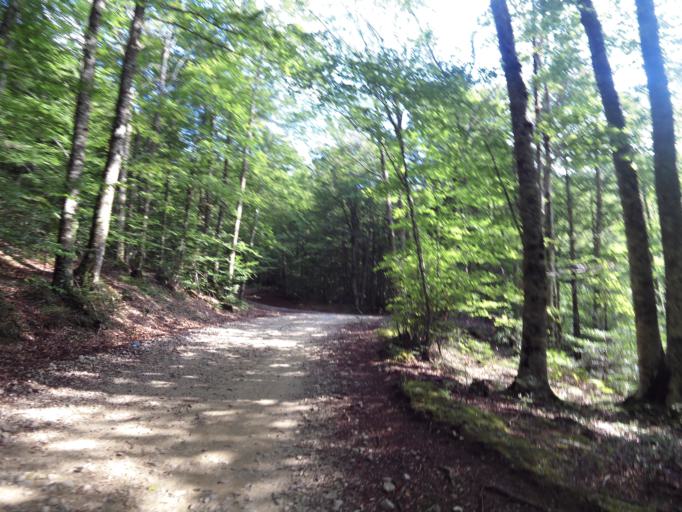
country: IT
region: Calabria
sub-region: Provincia di Vibo-Valentia
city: Mongiana
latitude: 38.5239
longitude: 16.3810
